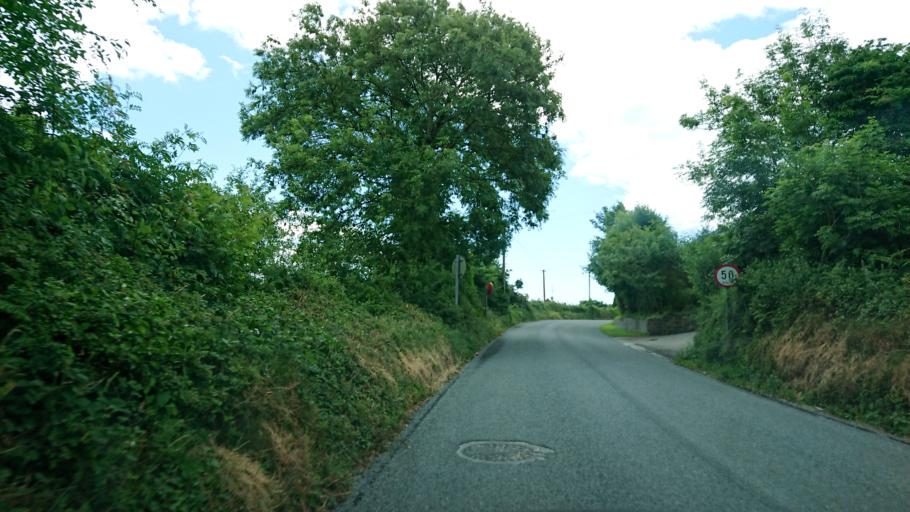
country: IE
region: Munster
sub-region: Waterford
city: Tra Mhor
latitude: 52.1756
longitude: -7.1412
